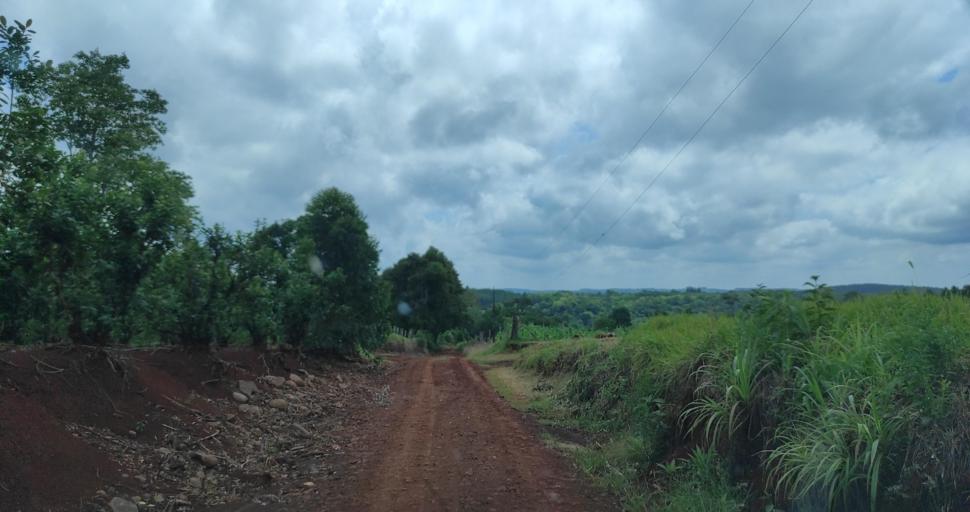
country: AR
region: Misiones
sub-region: Departamento de Veinticinco de Mayo
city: Veinticinco de Mayo
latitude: -27.4156
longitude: -54.7276
